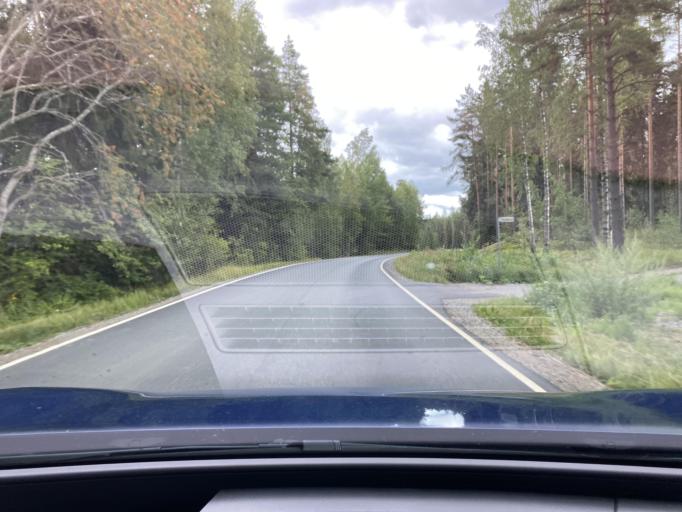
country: FI
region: Pirkanmaa
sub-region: Lounais-Pirkanmaa
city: Vammala
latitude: 61.3010
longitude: 22.9632
